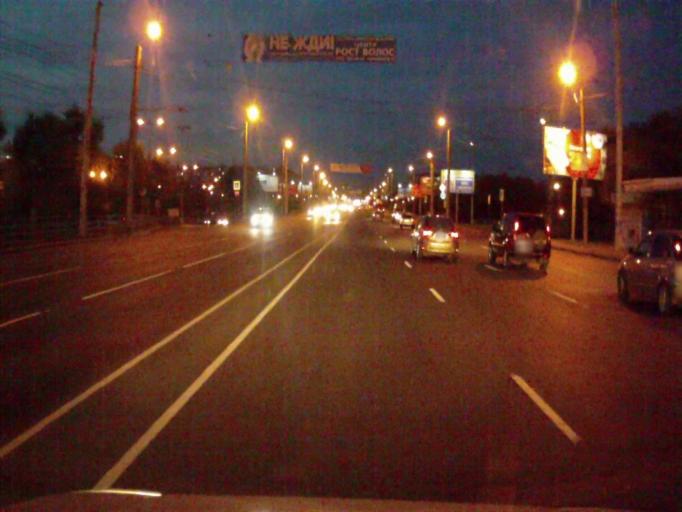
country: RU
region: Chelyabinsk
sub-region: Gorod Chelyabinsk
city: Chelyabinsk
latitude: 55.1716
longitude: 61.3582
